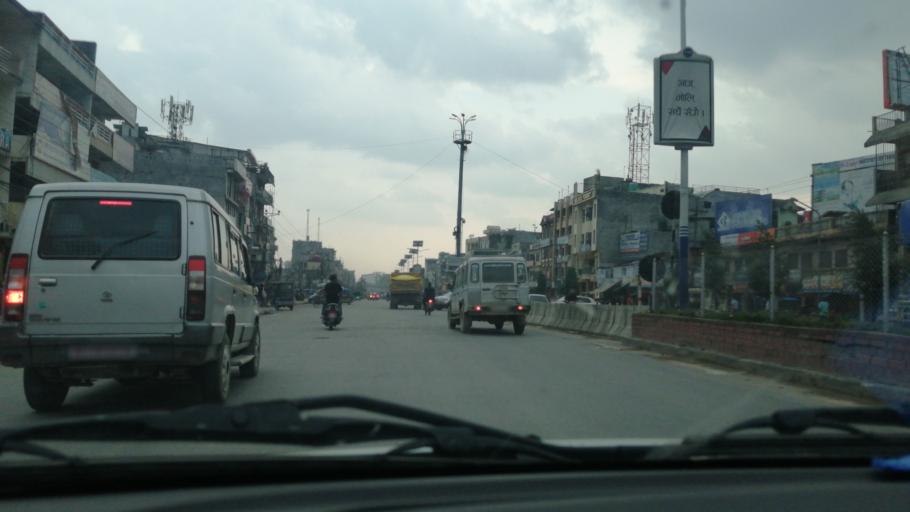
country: NP
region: Western Region
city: Butwal
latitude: 27.7025
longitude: 83.4665
